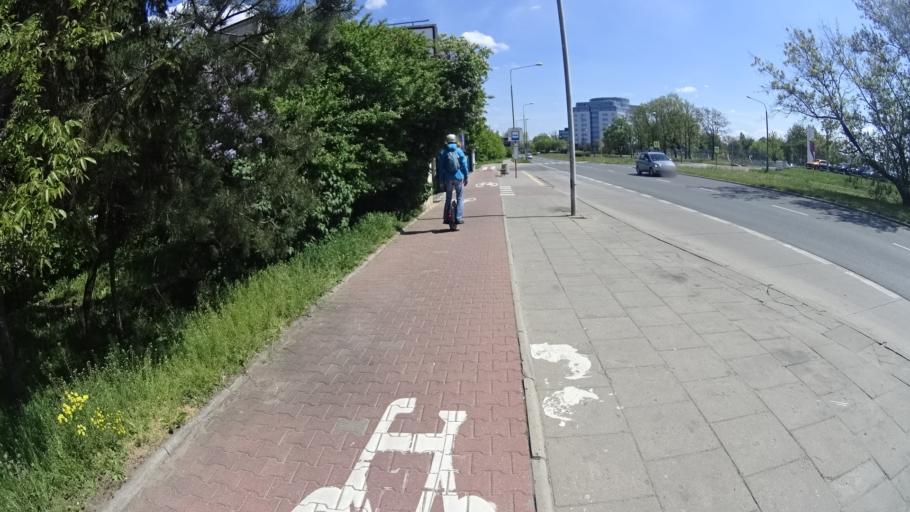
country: PL
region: Masovian Voivodeship
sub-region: Warszawa
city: Wlochy
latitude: 52.1848
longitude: 20.9597
